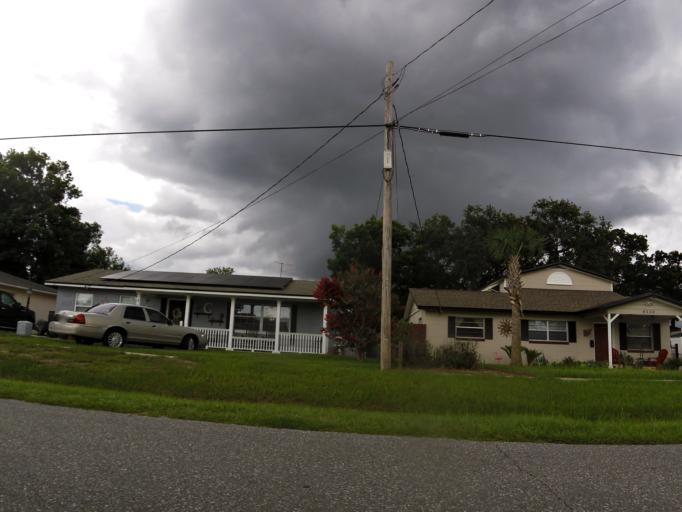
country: US
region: Florida
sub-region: Duval County
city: Jacksonville
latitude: 30.2747
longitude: -81.7234
